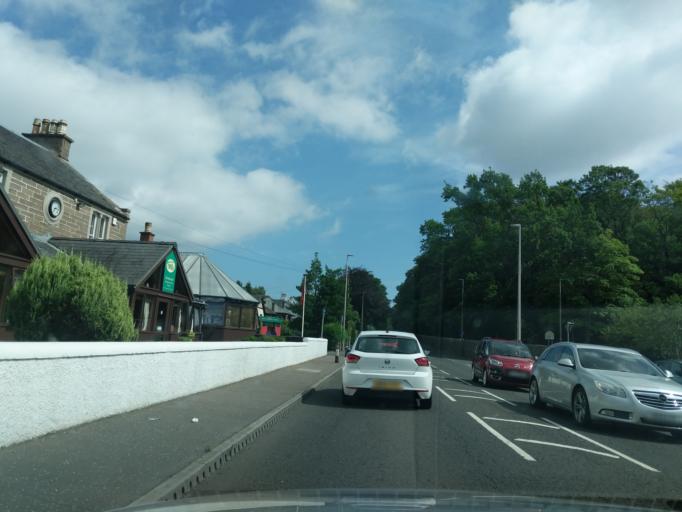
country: GB
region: Scotland
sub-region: Angus
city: Muirhead
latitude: 56.4928
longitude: -3.0520
